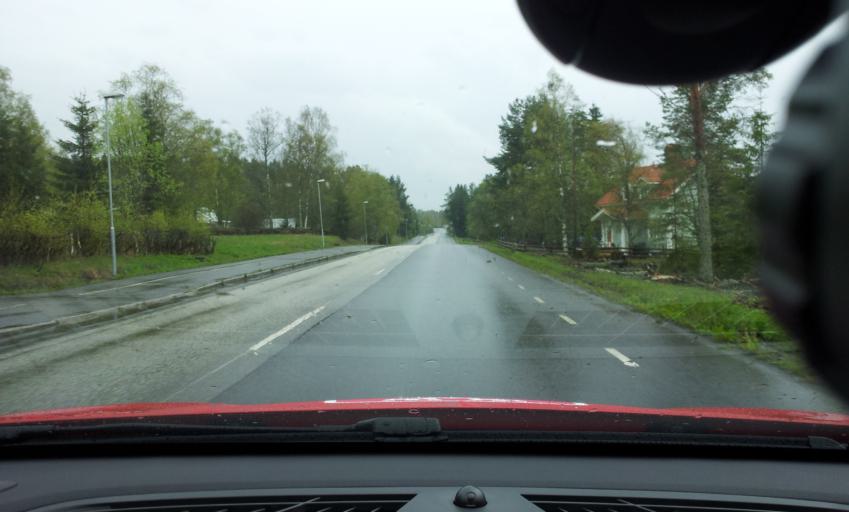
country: SE
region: Jaemtland
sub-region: OEstersunds Kommun
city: Brunflo
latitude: 63.1122
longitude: 14.7900
